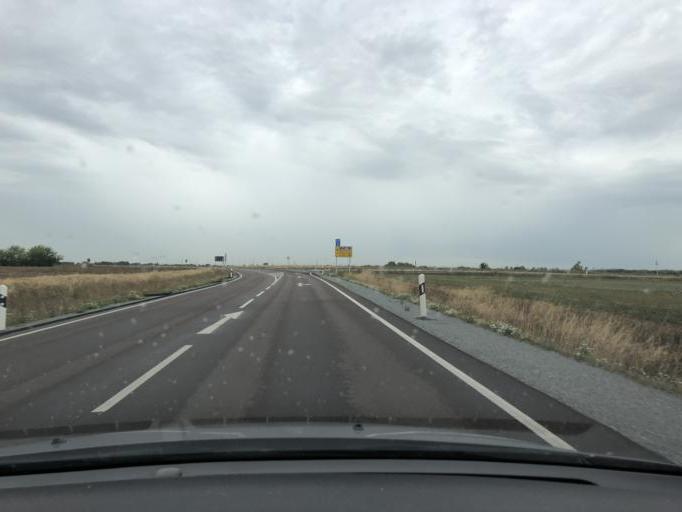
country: DE
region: Saxony-Anhalt
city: Brumby
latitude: 51.8937
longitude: 11.7023
